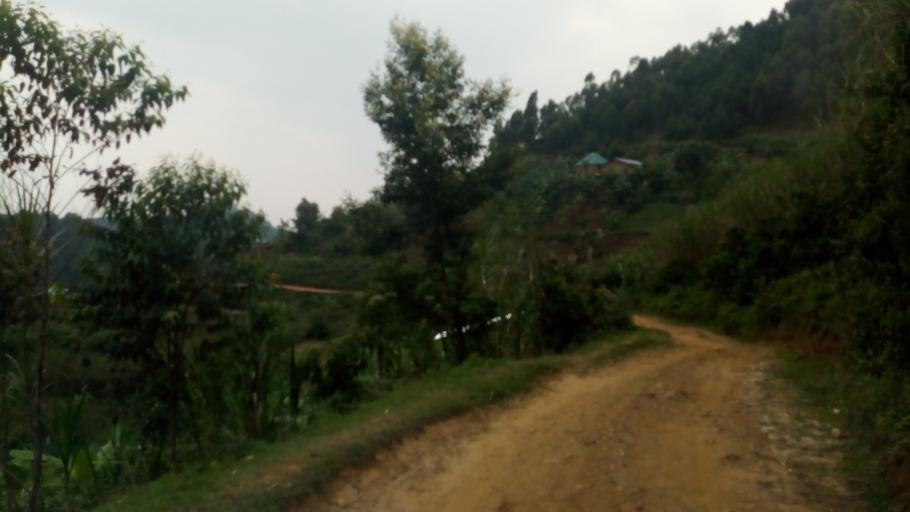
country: UG
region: Western Region
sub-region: Kisoro District
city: Kisoro
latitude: -1.2404
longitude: 29.6154
